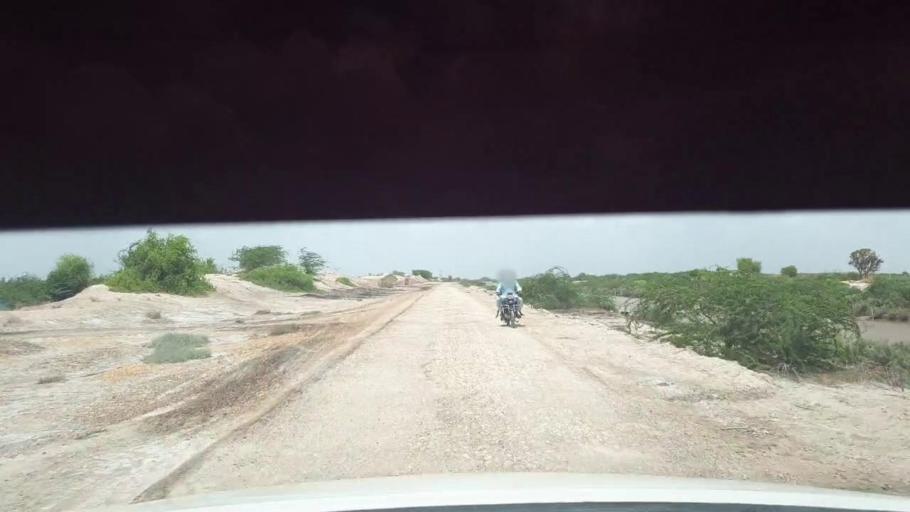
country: PK
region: Sindh
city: Kadhan
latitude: 24.5162
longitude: 69.1206
